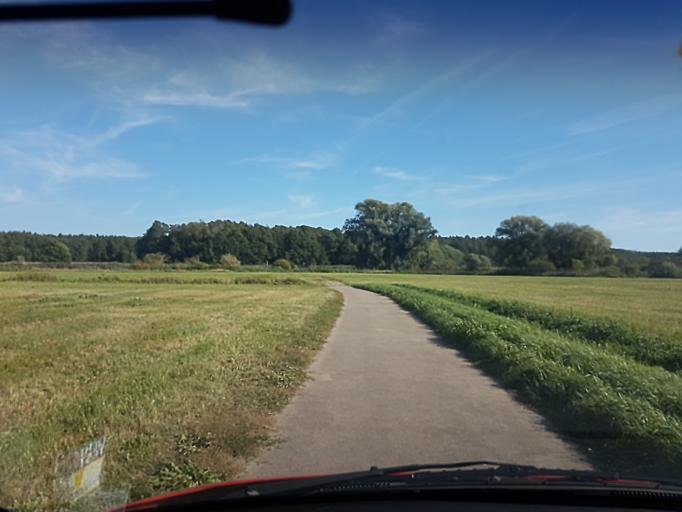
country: DE
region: Bavaria
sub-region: Upper Franconia
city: Hallerndorf
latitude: 49.7318
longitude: 10.9428
